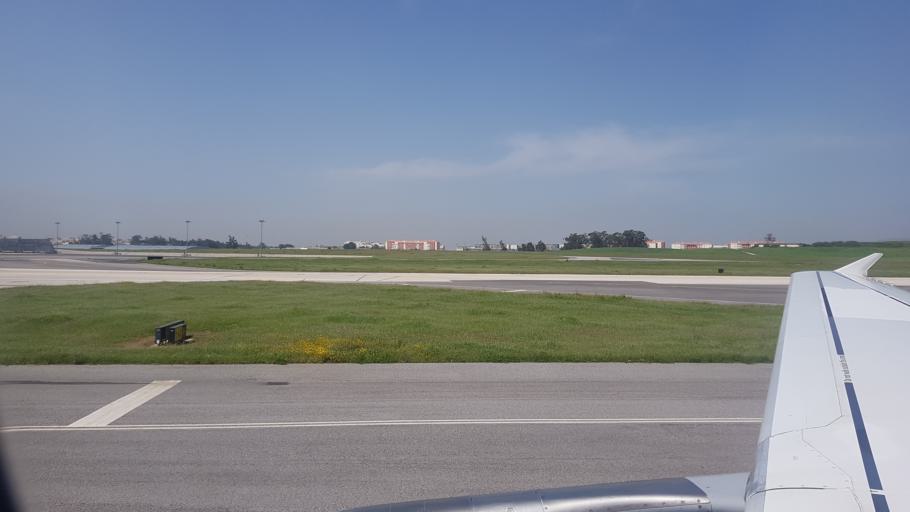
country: PT
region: Lisbon
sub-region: Loures
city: Camarate
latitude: 38.7759
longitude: -9.1333
